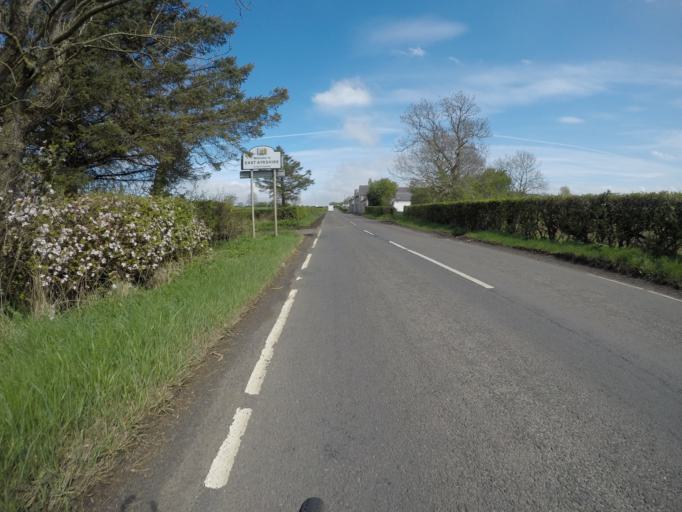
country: GB
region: Scotland
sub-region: East Ayrshire
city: Stewarton
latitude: 55.6667
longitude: -4.5371
